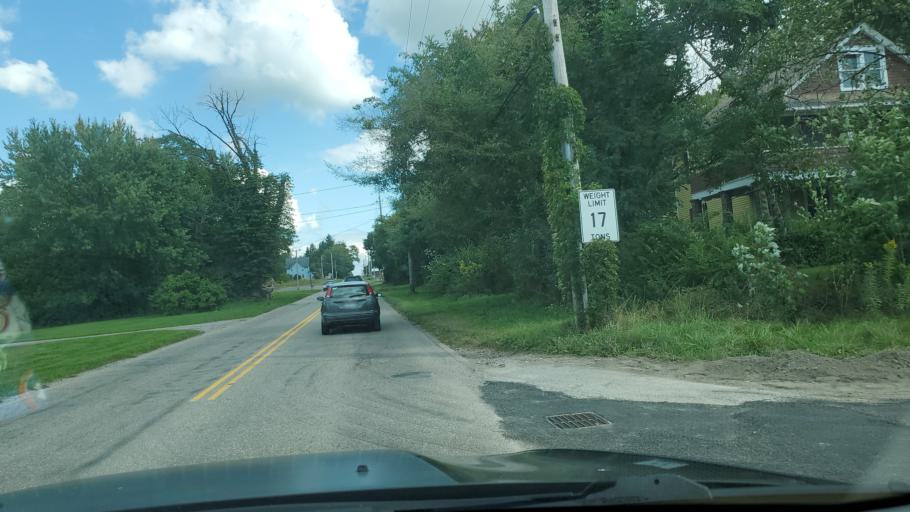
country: US
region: Ohio
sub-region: Mahoning County
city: Boardman
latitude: 40.9879
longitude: -80.6515
